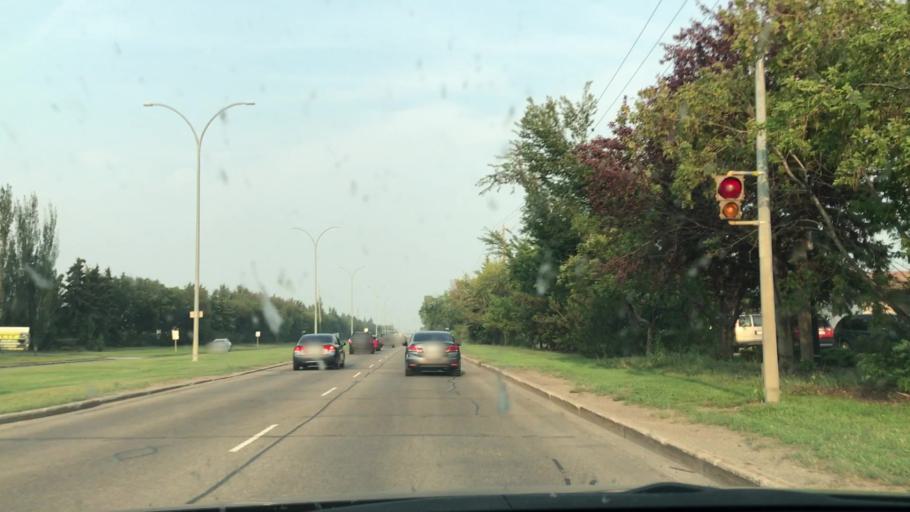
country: CA
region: Alberta
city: Edmonton
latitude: 53.5996
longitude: -113.4654
